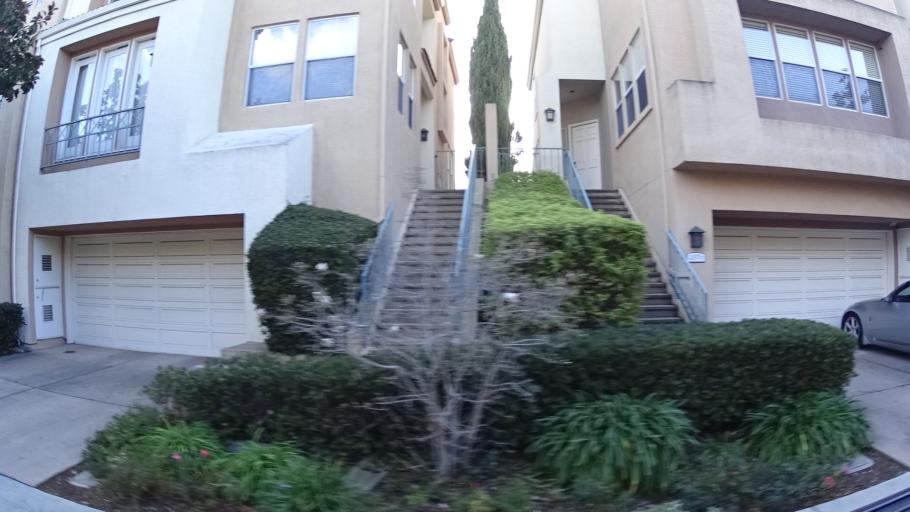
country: US
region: California
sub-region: Santa Clara County
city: Cupertino
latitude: 37.3371
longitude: -122.0302
